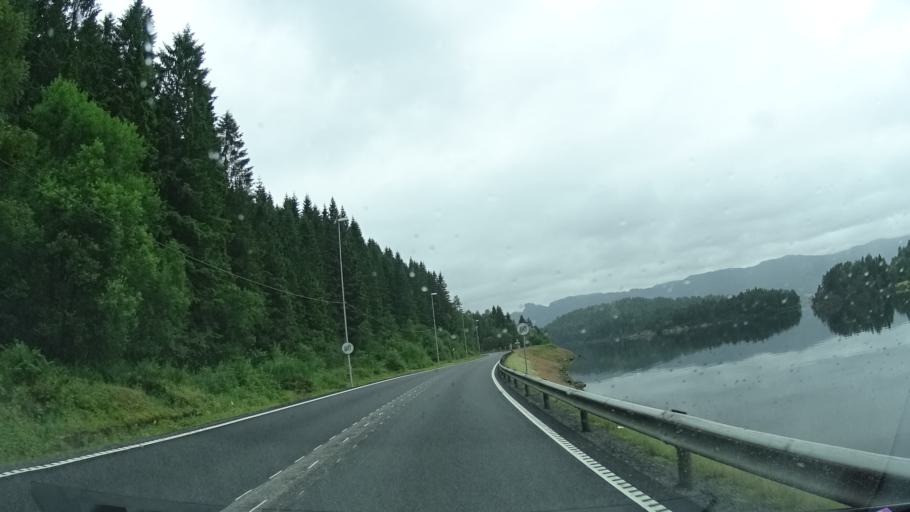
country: NO
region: Rogaland
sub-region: Lund
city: Moi
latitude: 58.4392
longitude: 6.6091
